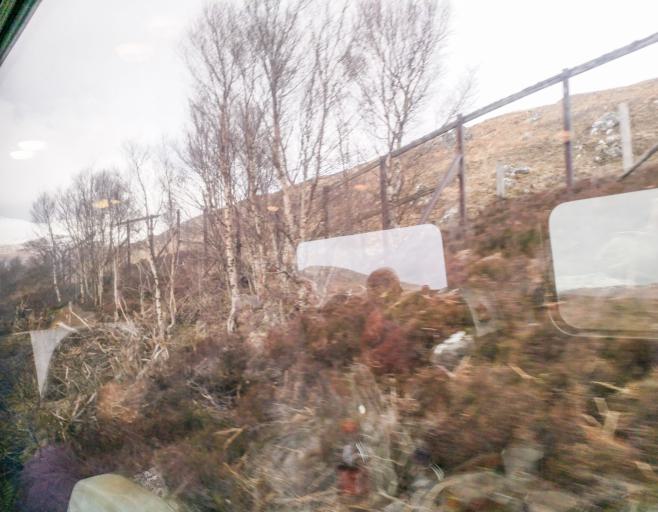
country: GB
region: Scotland
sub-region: Highland
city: Spean Bridge
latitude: 56.7760
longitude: -4.7295
